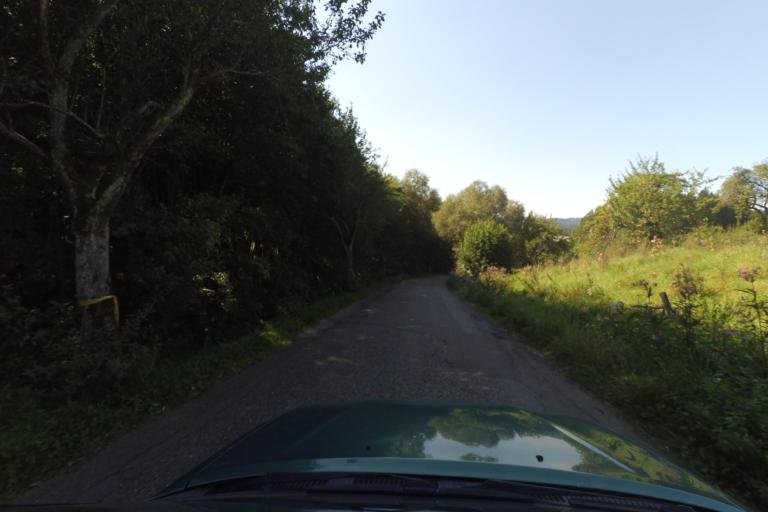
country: DE
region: Baden-Wuerttemberg
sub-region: Regierungsbezirk Stuttgart
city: Ruppertshofen
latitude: 48.8881
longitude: 9.8063
